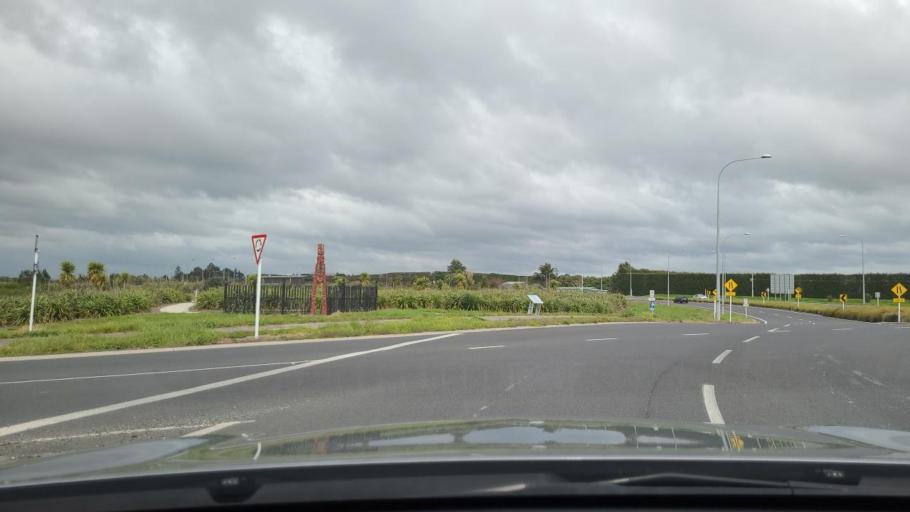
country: NZ
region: Bay of Plenty
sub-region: Western Bay of Plenty District
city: Maketu
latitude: -37.8007
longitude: 176.3997
